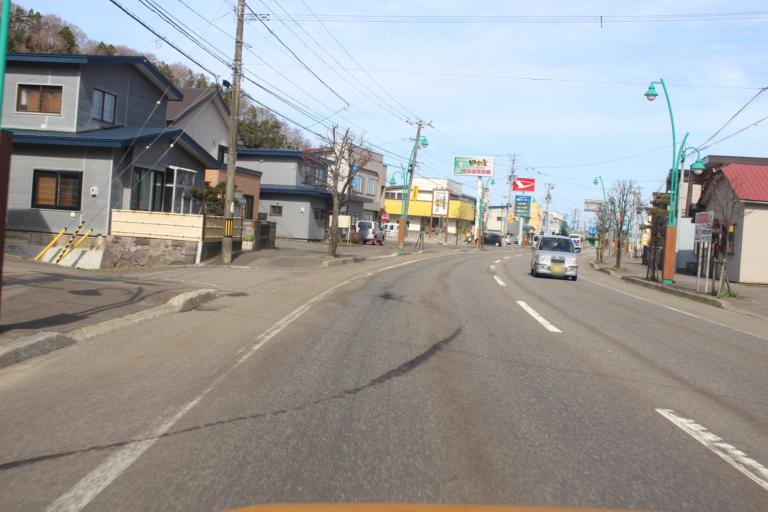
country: JP
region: Hokkaido
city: Kamiiso
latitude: 41.9154
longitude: 140.2259
